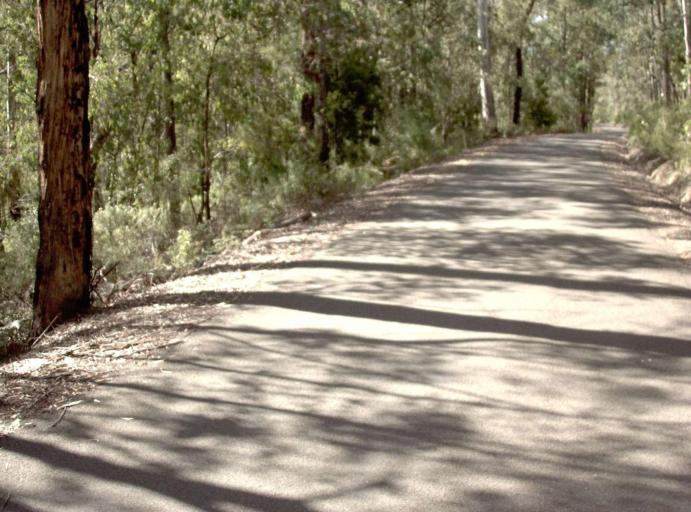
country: AU
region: Victoria
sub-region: East Gippsland
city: Lakes Entrance
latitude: -37.4613
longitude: 148.1221
